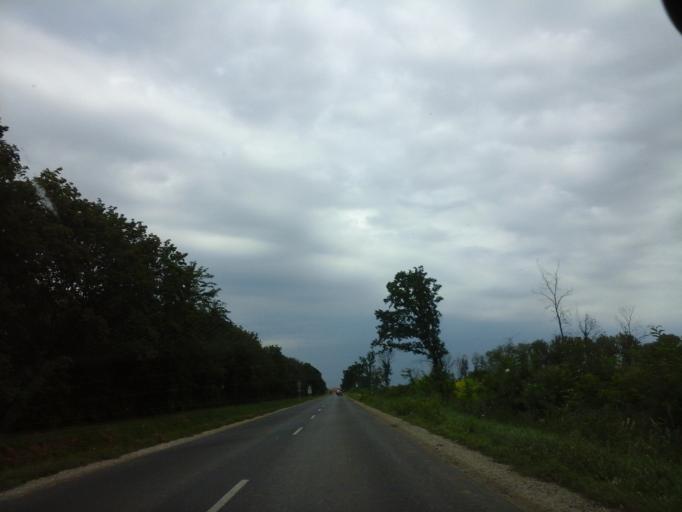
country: HU
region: Hajdu-Bihar
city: Balmazujvaros
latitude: 47.5930
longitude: 21.3416
